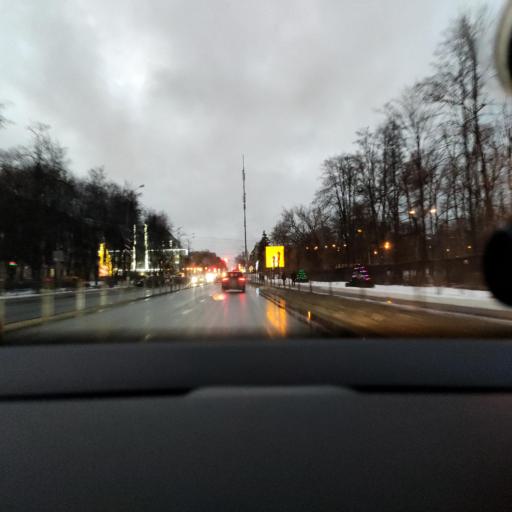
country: RU
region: Moskovskaya
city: Mytishchi
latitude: 55.9087
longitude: 37.7397
